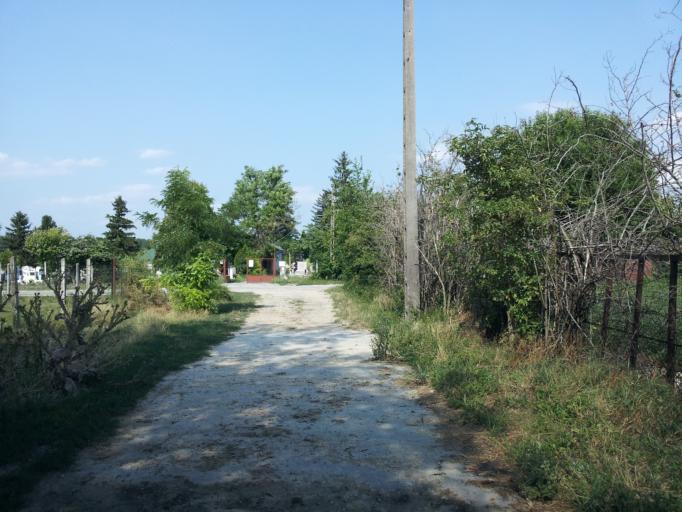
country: HU
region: Veszprem
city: Balatonkenese
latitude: 47.0816
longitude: 18.0873
